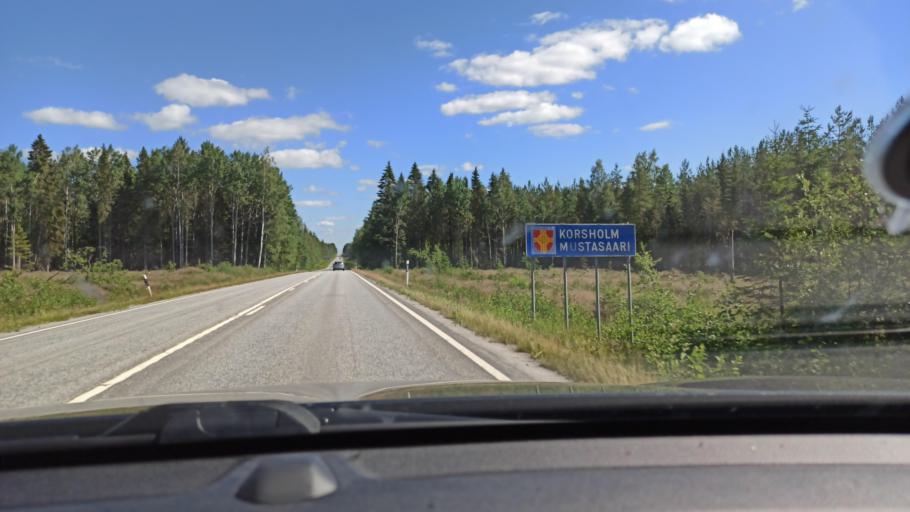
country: FI
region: Ostrobothnia
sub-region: Vaasa
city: Malax
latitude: 62.9740
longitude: 21.6005
